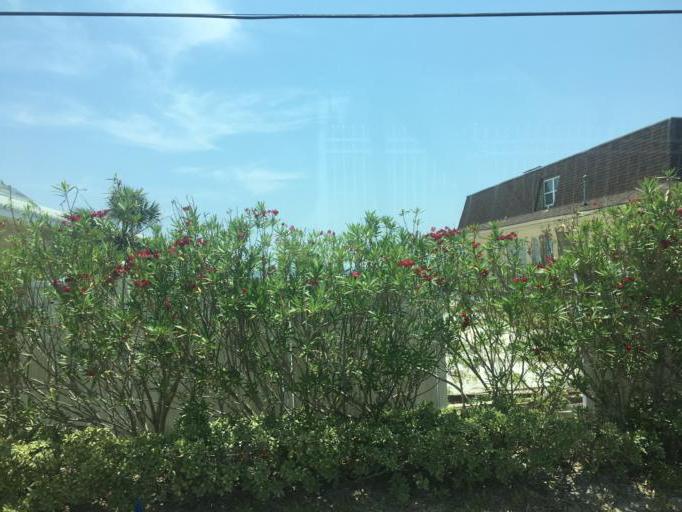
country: US
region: Florida
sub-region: Bay County
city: Lower Grand Lagoon
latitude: 30.1445
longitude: -85.7583
